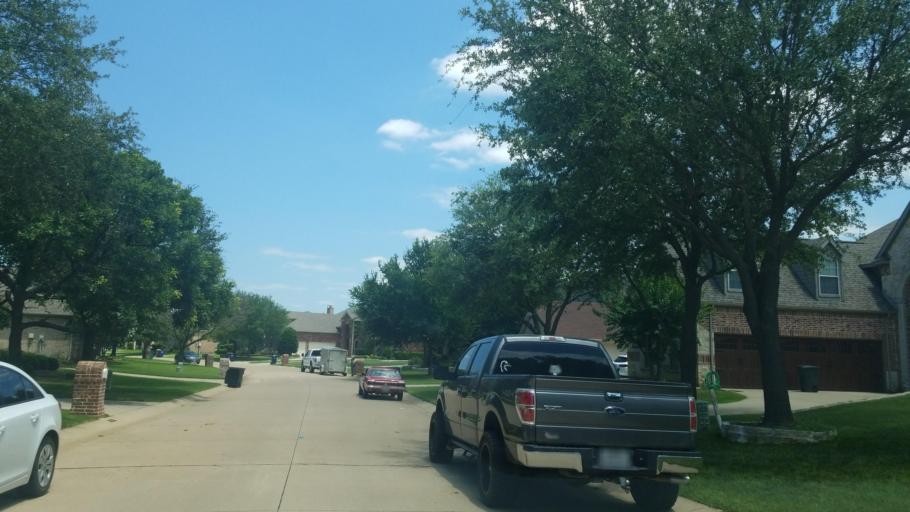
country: US
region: Texas
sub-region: Denton County
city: Copper Canyon
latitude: 33.0763
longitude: -97.0844
